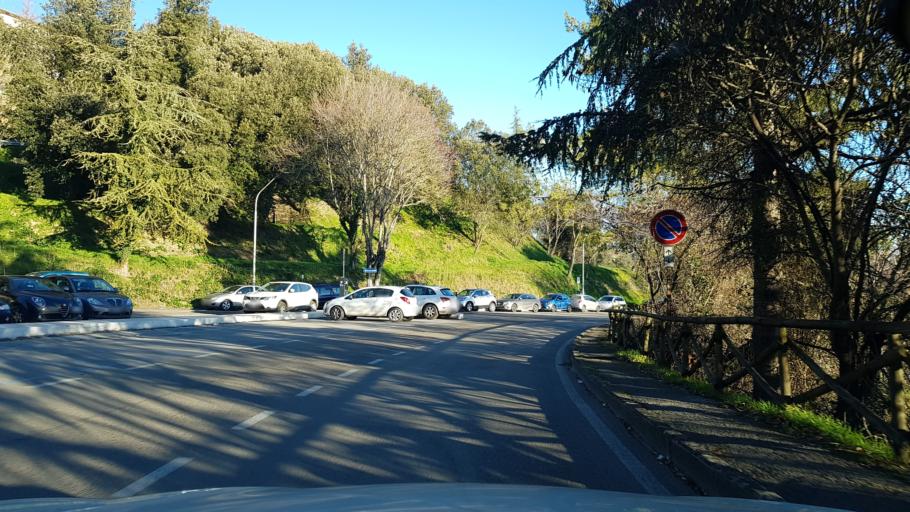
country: IT
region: Umbria
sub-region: Provincia di Perugia
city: Perugia
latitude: 43.1061
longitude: 12.3936
